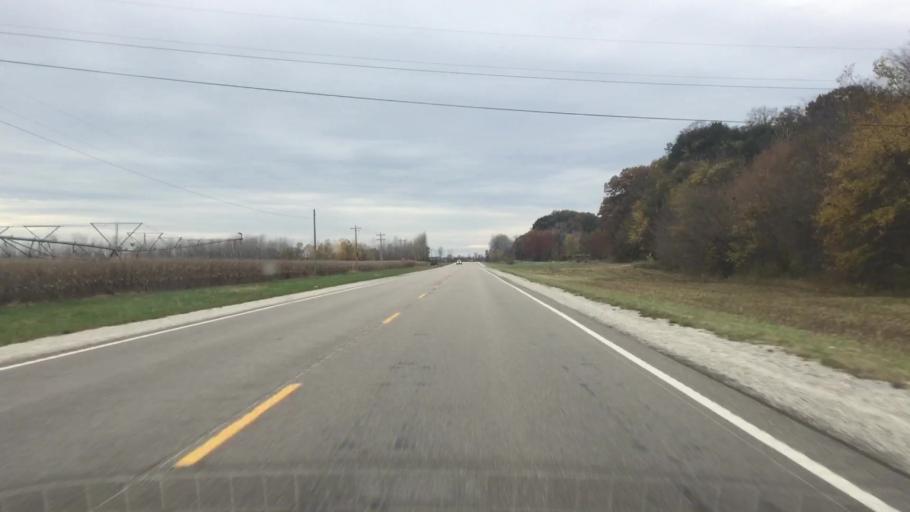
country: US
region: Missouri
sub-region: Callaway County
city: Holts Summit
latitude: 38.5815
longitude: -92.1036
